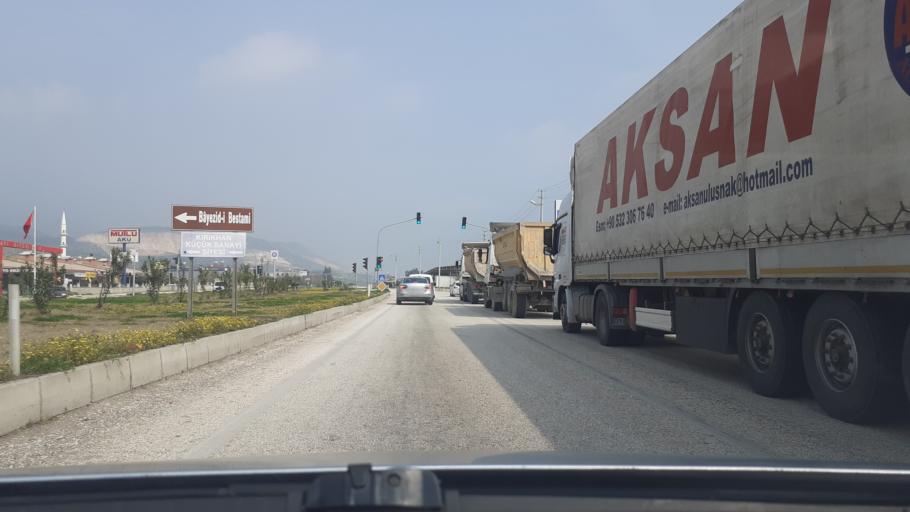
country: TR
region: Hatay
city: Kirikhan
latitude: 36.5227
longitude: 36.3772
